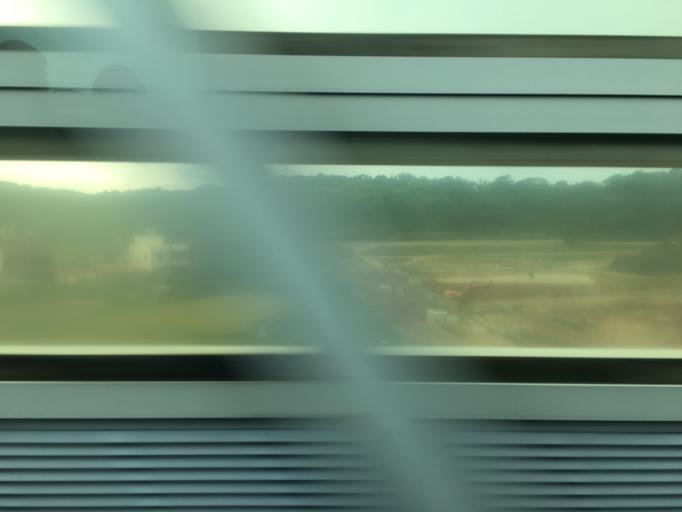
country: TW
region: Taiwan
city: Taoyuan City
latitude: 25.0809
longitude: 121.2915
